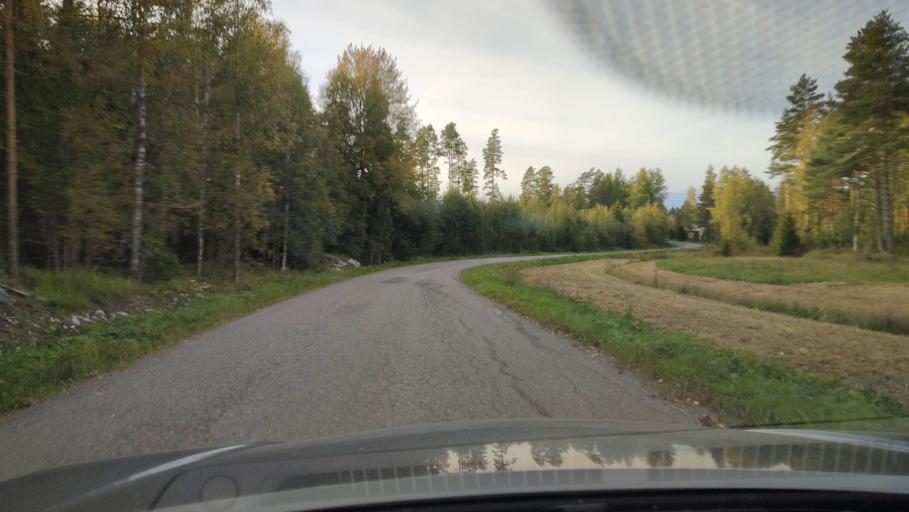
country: FI
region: Southern Ostrobothnia
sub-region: Suupohja
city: Karijoki
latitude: 62.1365
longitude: 21.5732
